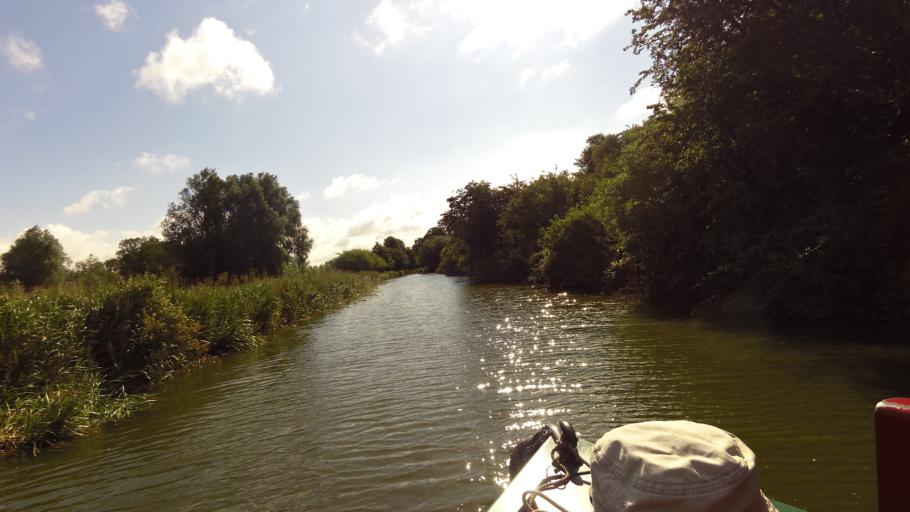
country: GB
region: England
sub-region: West Berkshire
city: Hungerford
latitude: 51.4116
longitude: -1.4891
